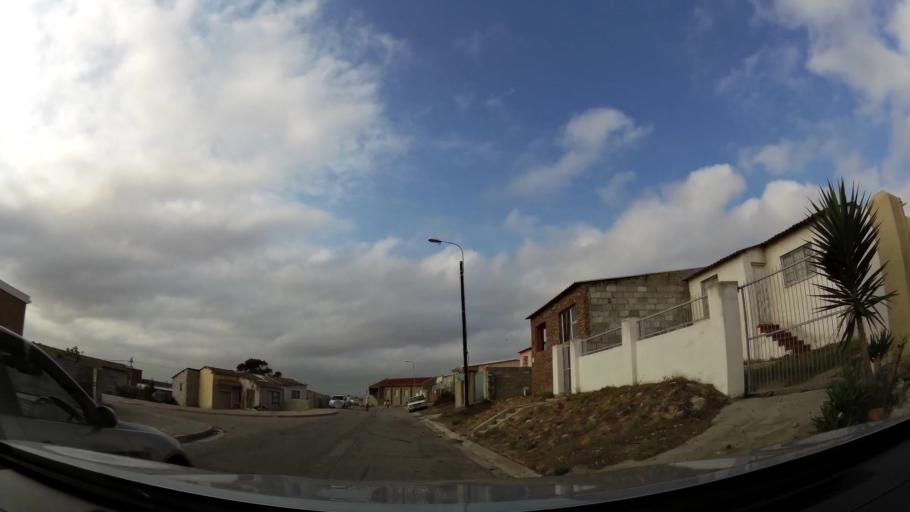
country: ZA
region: Eastern Cape
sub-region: Nelson Mandela Bay Metropolitan Municipality
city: Port Elizabeth
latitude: -33.9188
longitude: 25.5445
